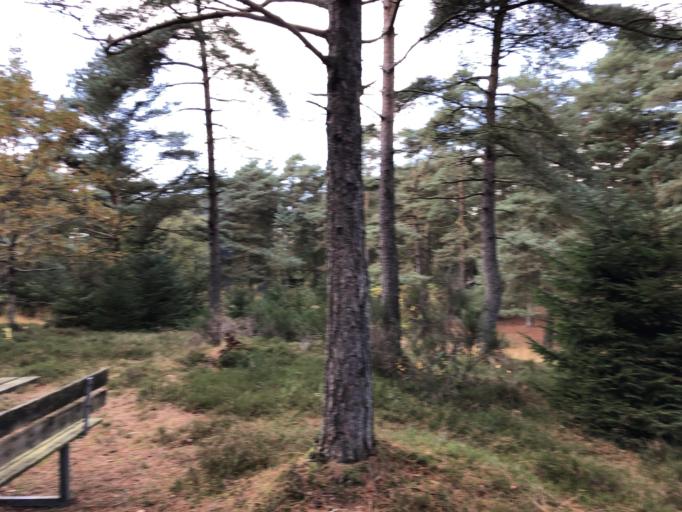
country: DK
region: Central Jutland
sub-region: Lemvig Kommune
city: Lemvig
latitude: 56.4869
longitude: 8.3030
